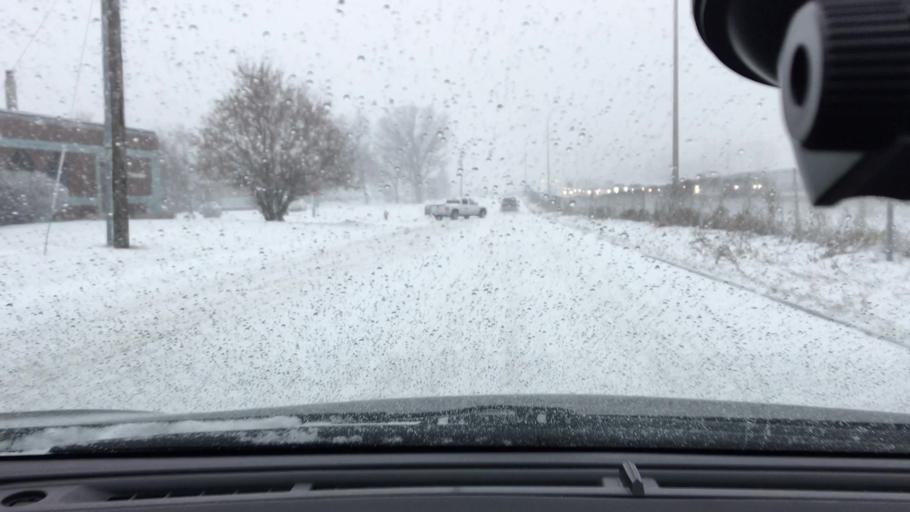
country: US
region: Minnesota
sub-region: Hennepin County
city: New Hope
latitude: 44.9874
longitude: -93.4004
